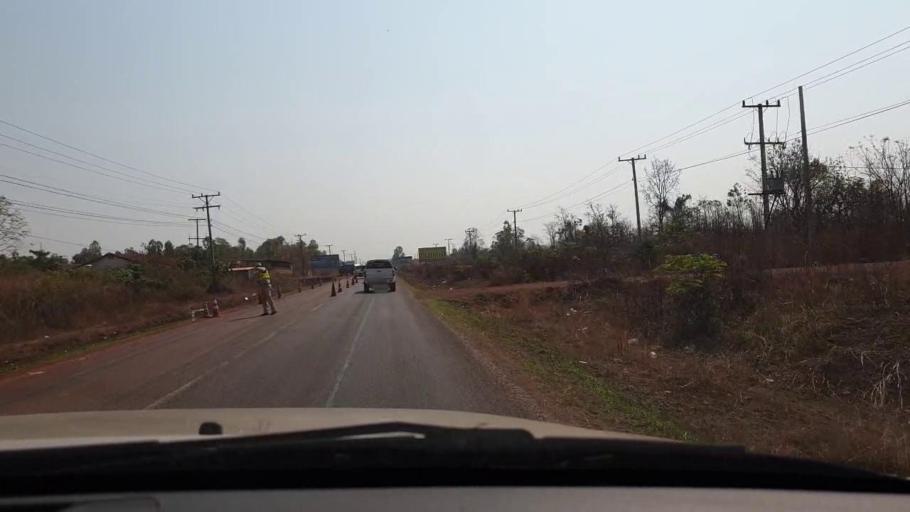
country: TH
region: Nong Khai
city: Nong Khai
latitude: 18.0531
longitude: 102.8435
